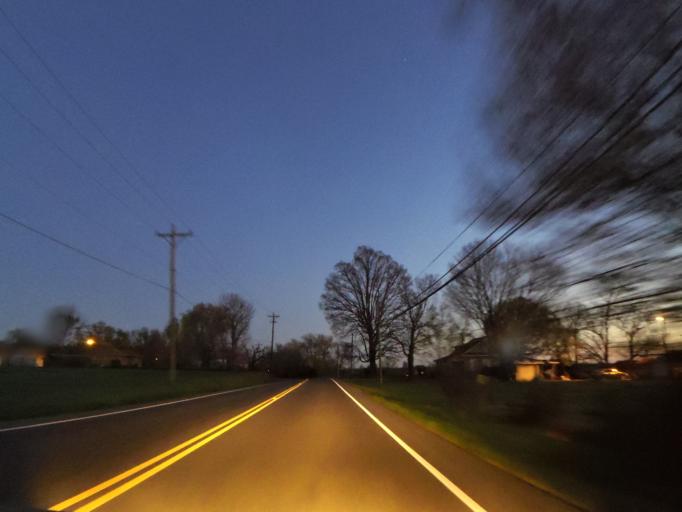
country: US
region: Tennessee
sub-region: Robertson County
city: Ridgetop
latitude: 36.3416
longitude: -86.8716
